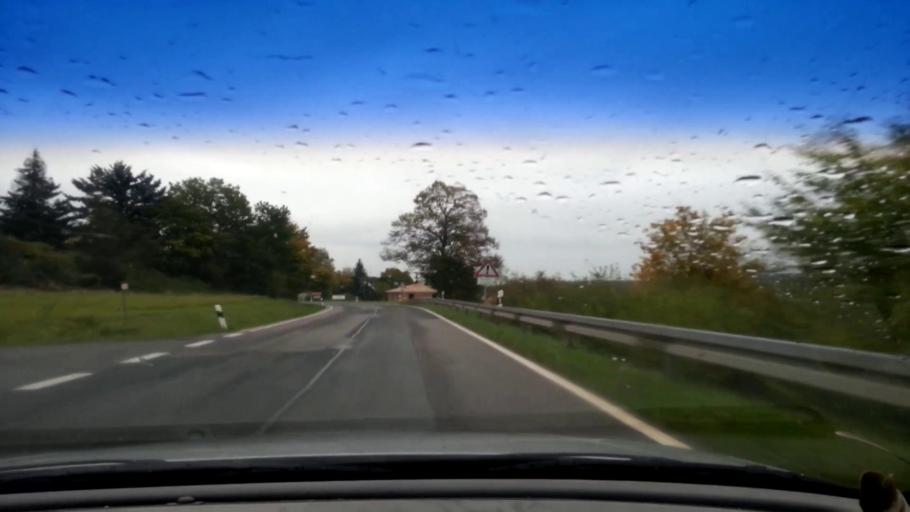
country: DE
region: Bavaria
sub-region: Upper Franconia
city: Priesendorf
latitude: 49.8596
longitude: 10.6838
